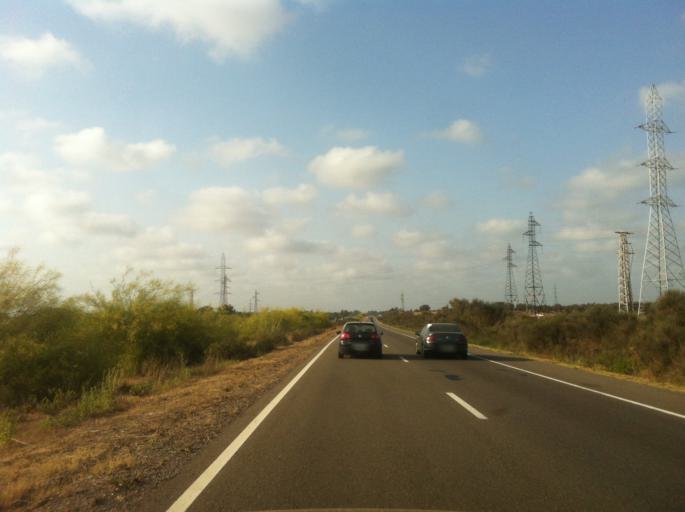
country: MA
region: Gharb-Chrarda-Beni Hssen
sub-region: Kenitra Province
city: Kenitra
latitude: 34.2279
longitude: -6.5568
